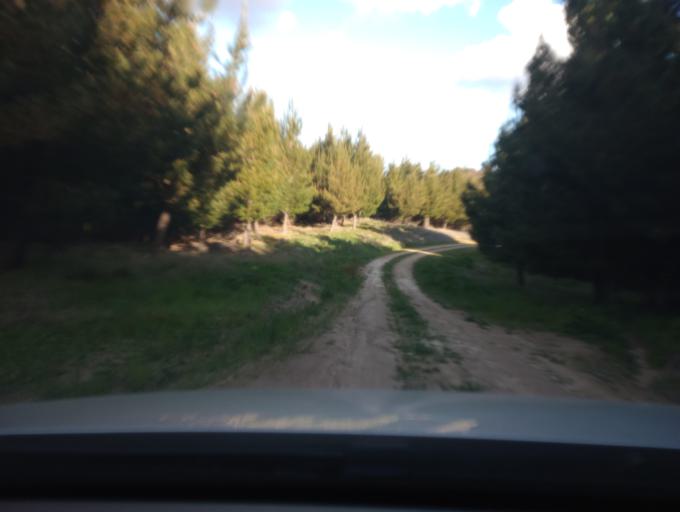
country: AU
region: New South Wales
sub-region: Blayney
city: Millthorpe
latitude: -33.4004
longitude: 149.3133
